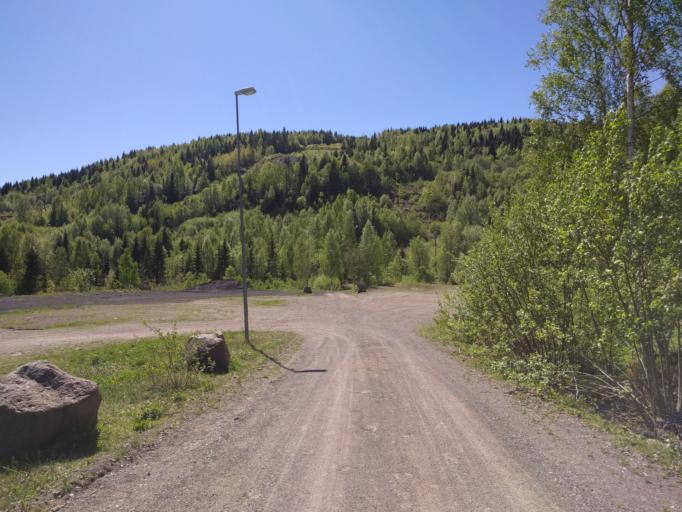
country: NO
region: Vestfold
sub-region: Lardal
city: Svarstad
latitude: 59.3988
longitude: 9.9285
